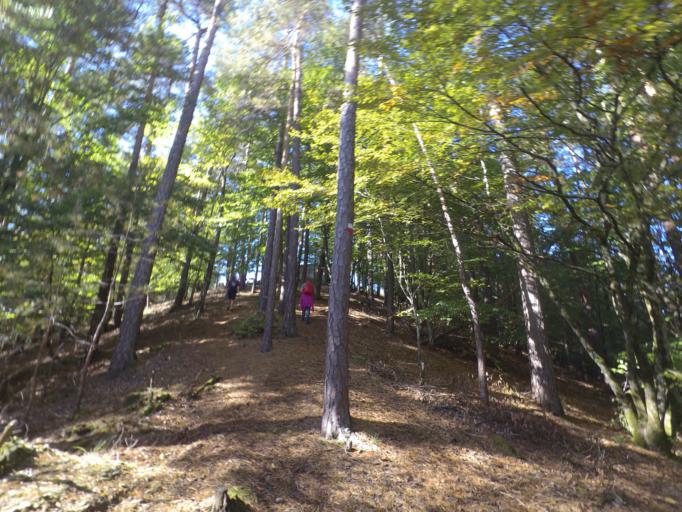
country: AT
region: Styria
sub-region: Politischer Bezirk Leibnitz
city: Kitzeck im Sausal
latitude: 46.7687
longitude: 15.4409
